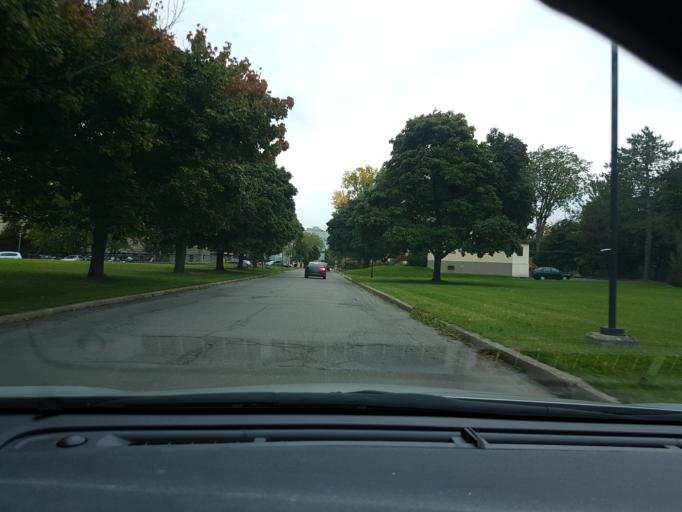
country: CA
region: Quebec
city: Quebec
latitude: 46.7910
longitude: -71.2610
